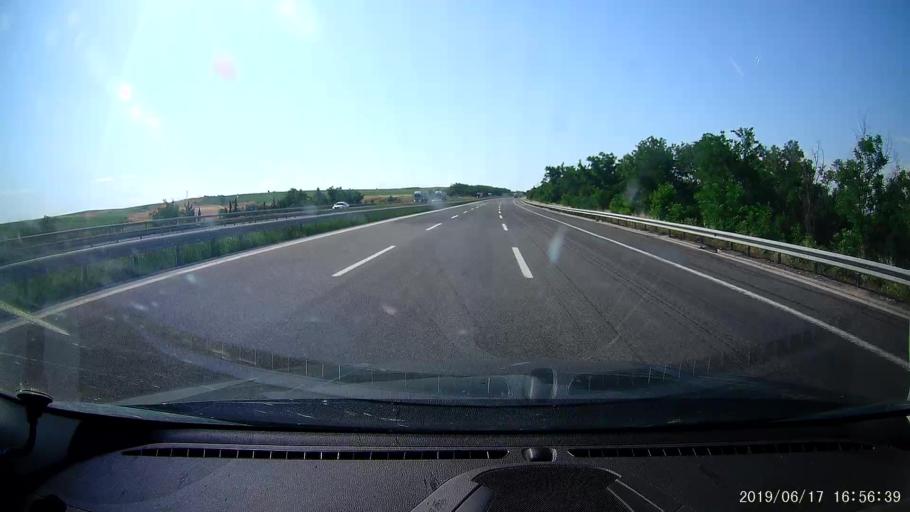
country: TR
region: Edirne
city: Haskoy
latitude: 41.5891
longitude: 26.9314
